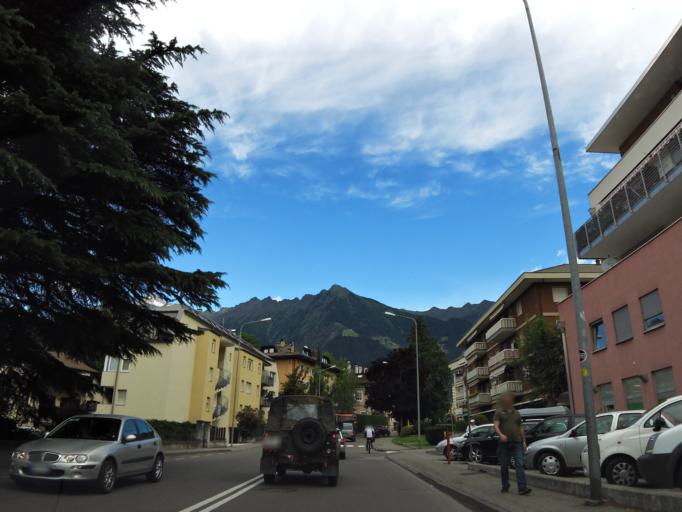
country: IT
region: Trentino-Alto Adige
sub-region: Bolzano
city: Merano
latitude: 46.6628
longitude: 11.1597
